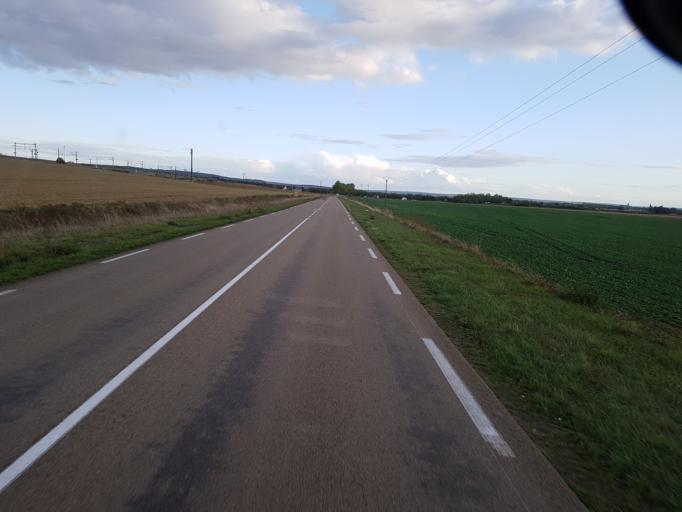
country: FR
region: Bourgogne
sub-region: Departement de l'Yonne
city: Soucy
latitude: 48.2668
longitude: 3.2785
